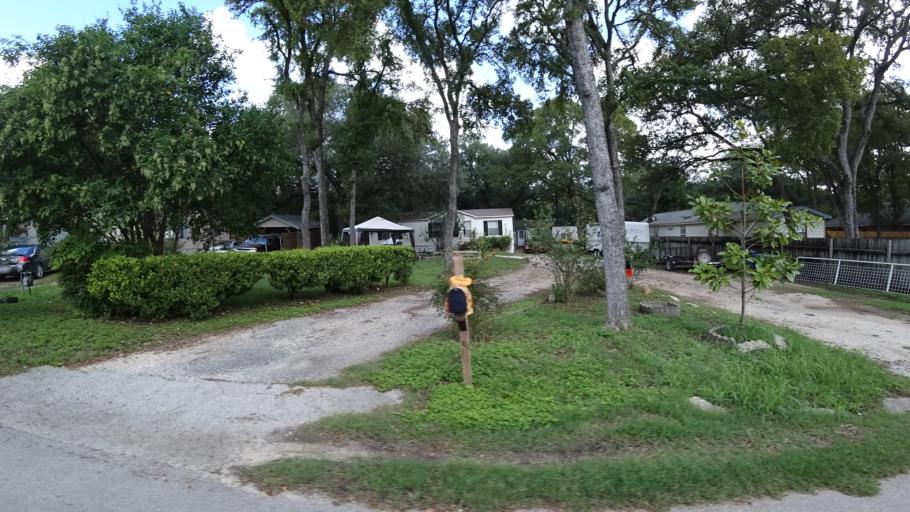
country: US
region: Texas
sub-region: Travis County
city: Onion Creek
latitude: 30.1887
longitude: -97.8007
